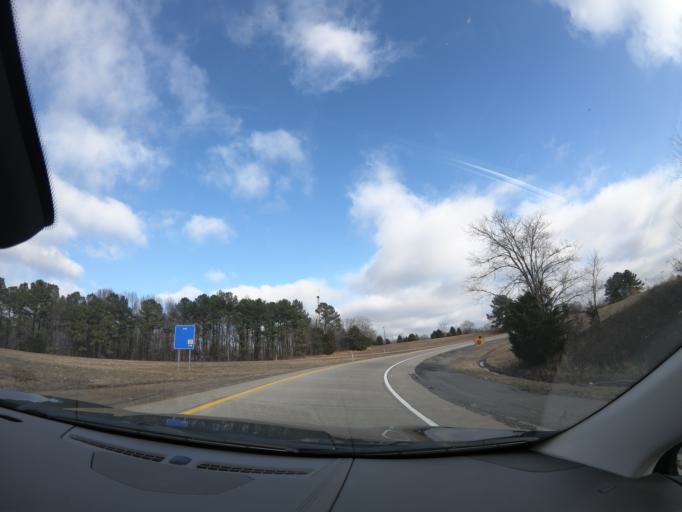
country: US
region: Tennessee
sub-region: Sumner County
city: Millersville
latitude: 36.4187
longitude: -86.7163
